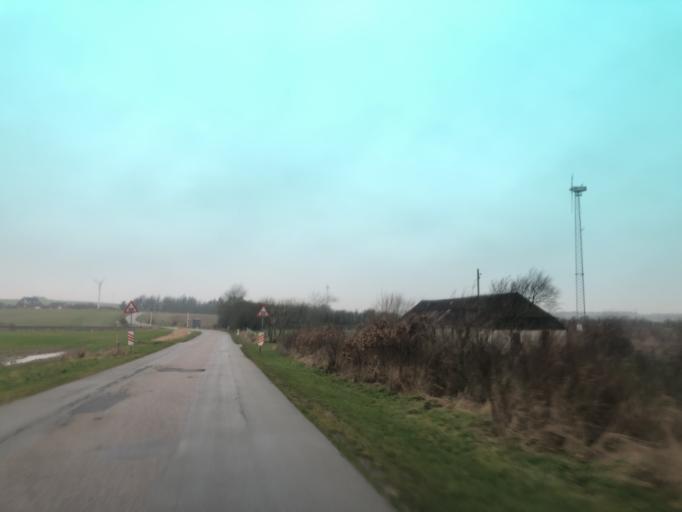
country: DK
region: North Denmark
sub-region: Thisted Kommune
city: Hurup
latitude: 56.7379
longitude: 8.4163
